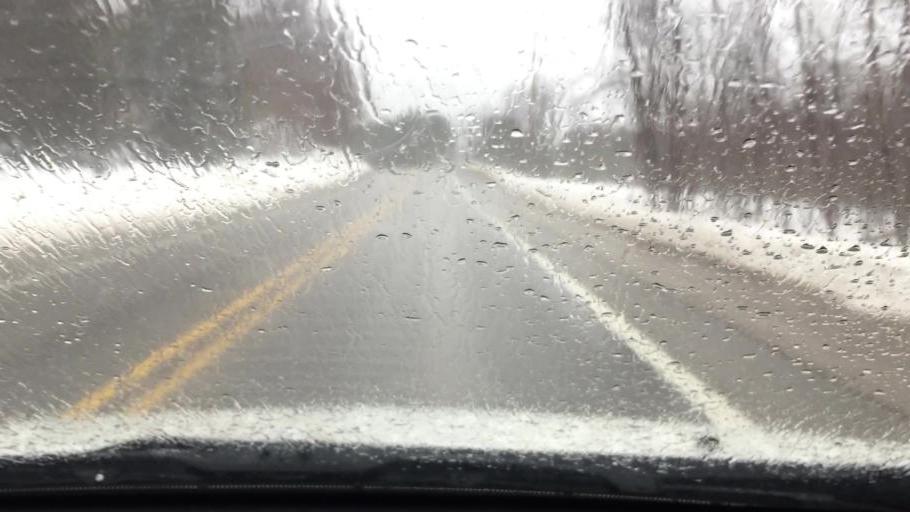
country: US
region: Michigan
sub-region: Charlevoix County
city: East Jordan
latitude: 45.2163
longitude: -85.1720
